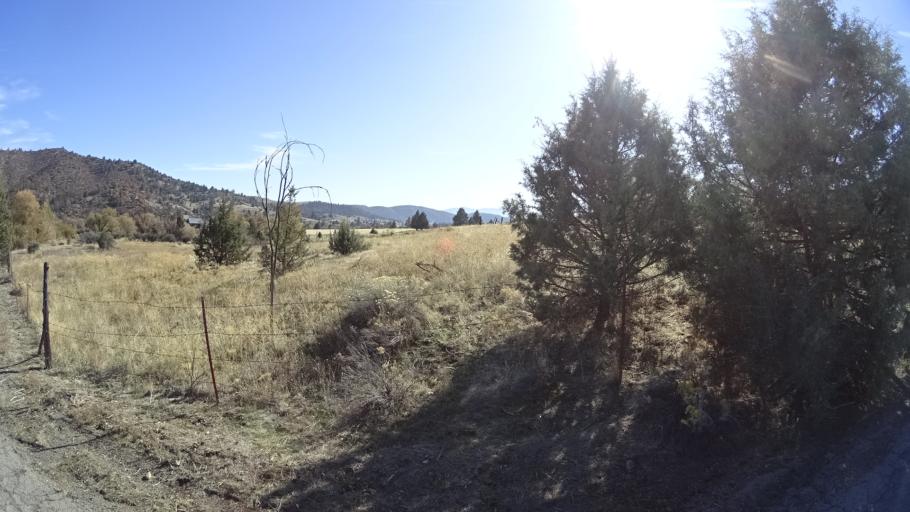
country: US
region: California
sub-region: Siskiyou County
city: Yreka
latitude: 41.7629
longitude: -122.6281
